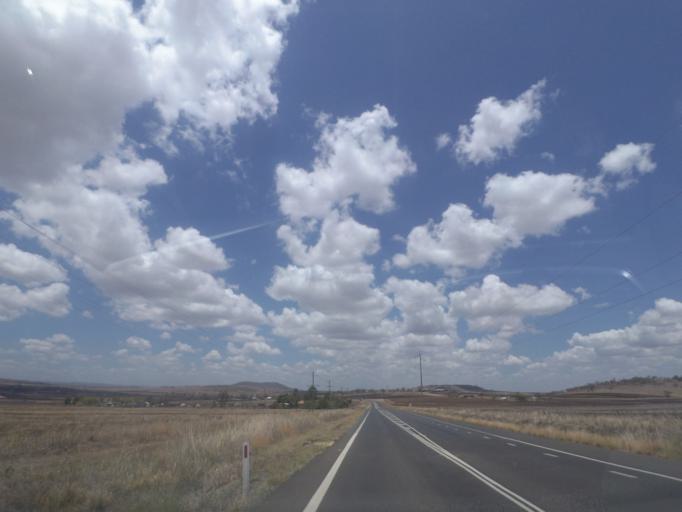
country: AU
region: Queensland
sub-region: Toowoomba
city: Top Camp
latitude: -27.7540
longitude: 151.9351
